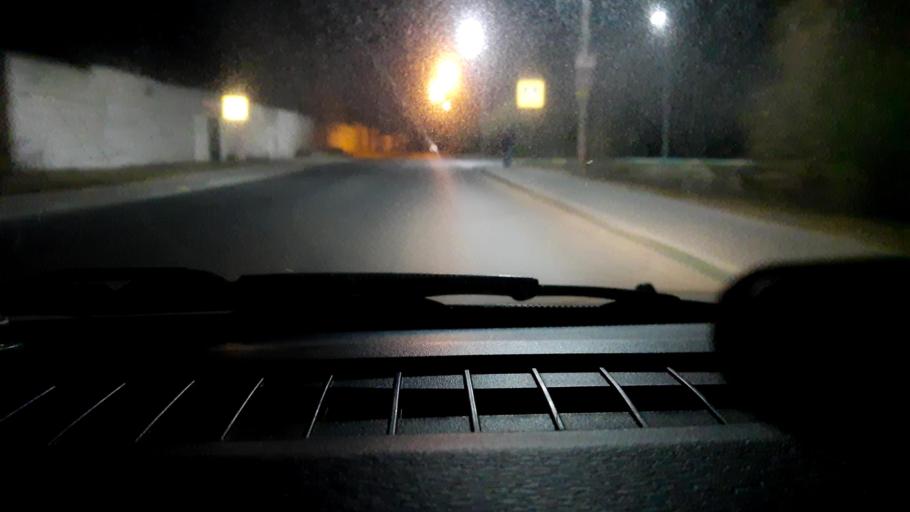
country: RU
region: Nizjnij Novgorod
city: Gorbatovka
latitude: 56.3599
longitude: 43.7976
